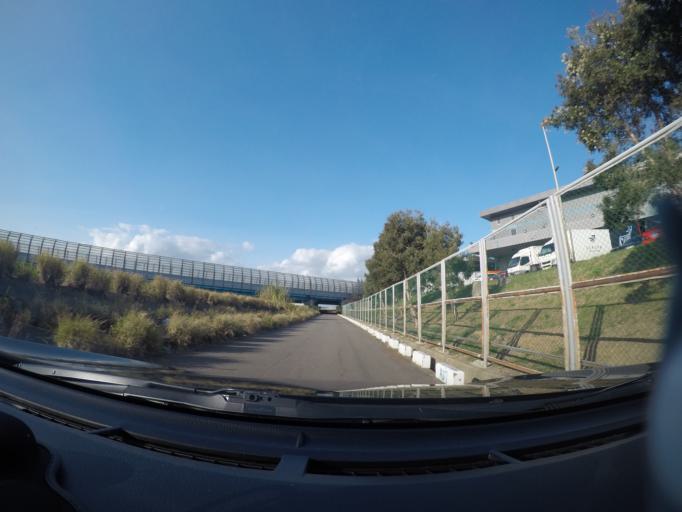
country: TW
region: Taiwan
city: Taoyuan City
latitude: 25.0978
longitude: 121.2515
